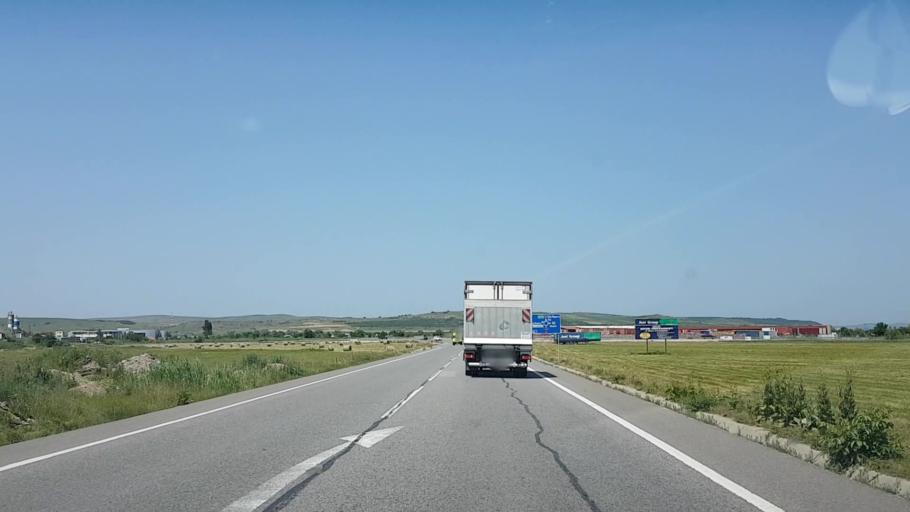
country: RO
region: Cluj
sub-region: Comuna Apahida
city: Dezmir
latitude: 46.7762
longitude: 23.7026
